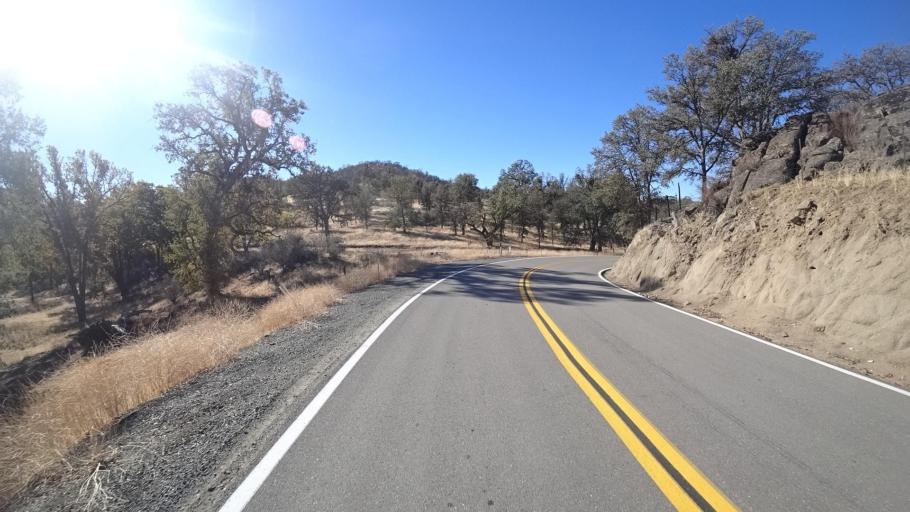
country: US
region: California
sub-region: Kern County
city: Alta Sierra
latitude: 35.7210
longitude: -118.6805
